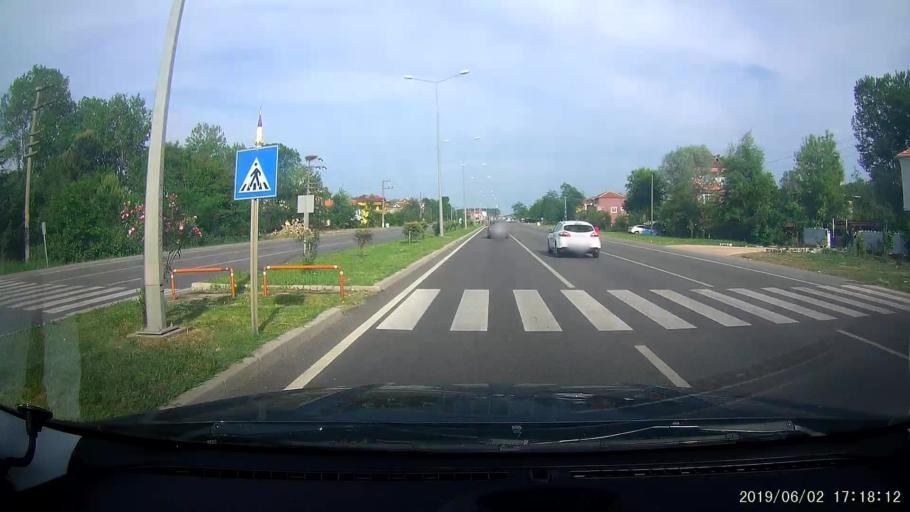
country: TR
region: Samsun
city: Dikbiyik
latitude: 41.2248
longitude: 36.5941
